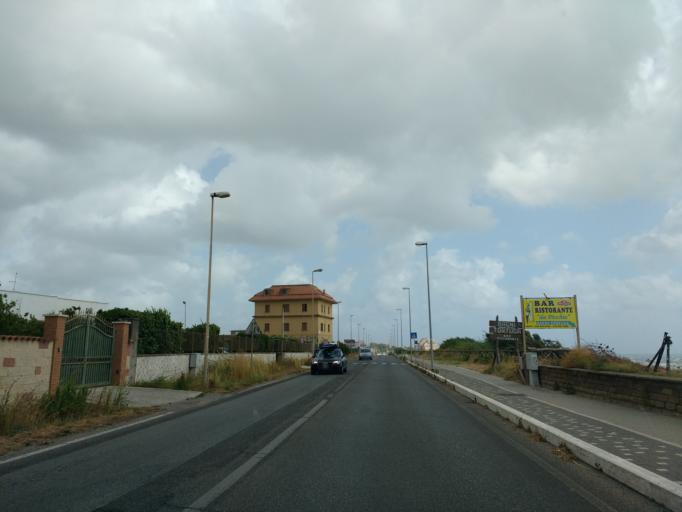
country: IT
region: Latium
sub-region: Citta metropolitana di Roma Capitale
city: Anzio
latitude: 41.4741
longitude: 12.6041
